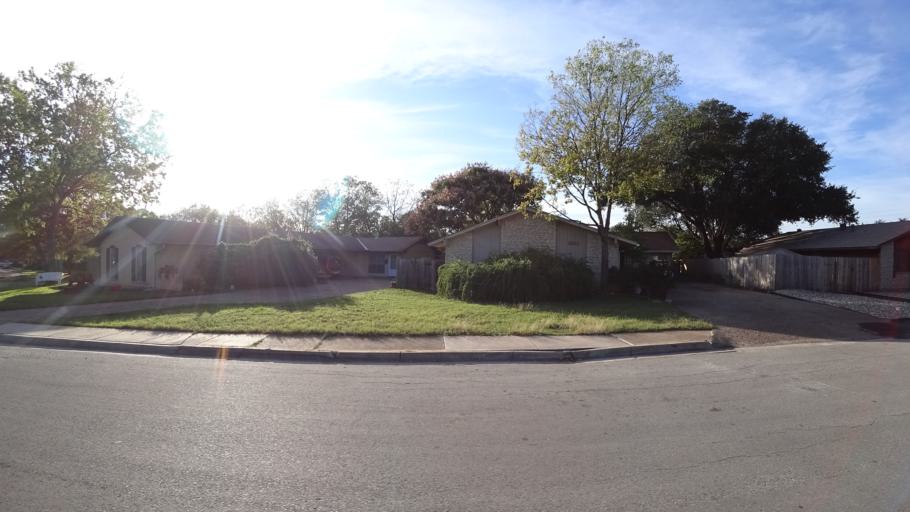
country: US
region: Texas
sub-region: Williamson County
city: Jollyville
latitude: 30.3746
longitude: -97.7345
